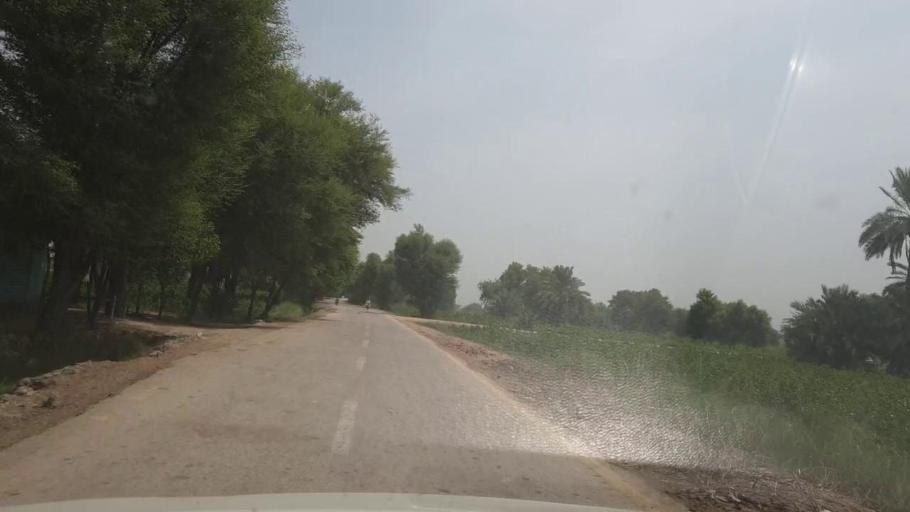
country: PK
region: Sindh
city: Kot Diji
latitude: 27.3726
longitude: 68.6499
